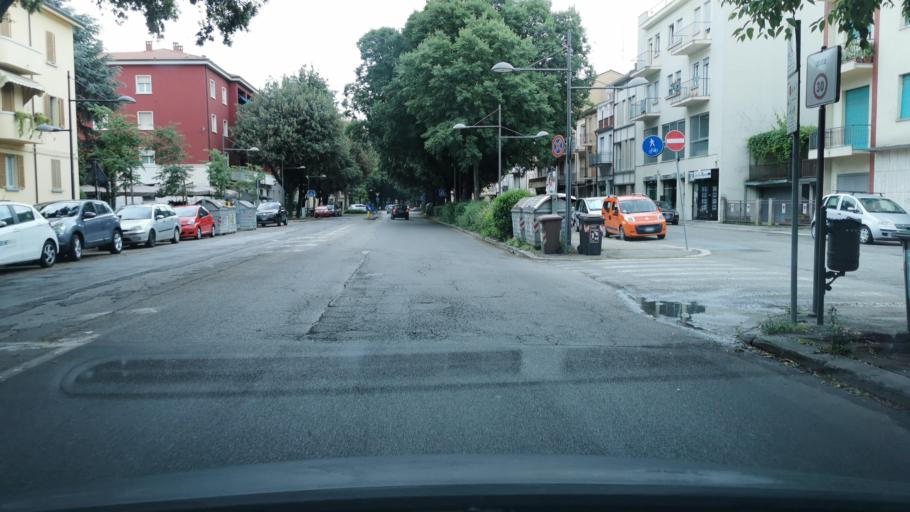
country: IT
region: Emilia-Romagna
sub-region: Provincia di Ravenna
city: Faenza
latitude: 44.2906
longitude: 11.8829
